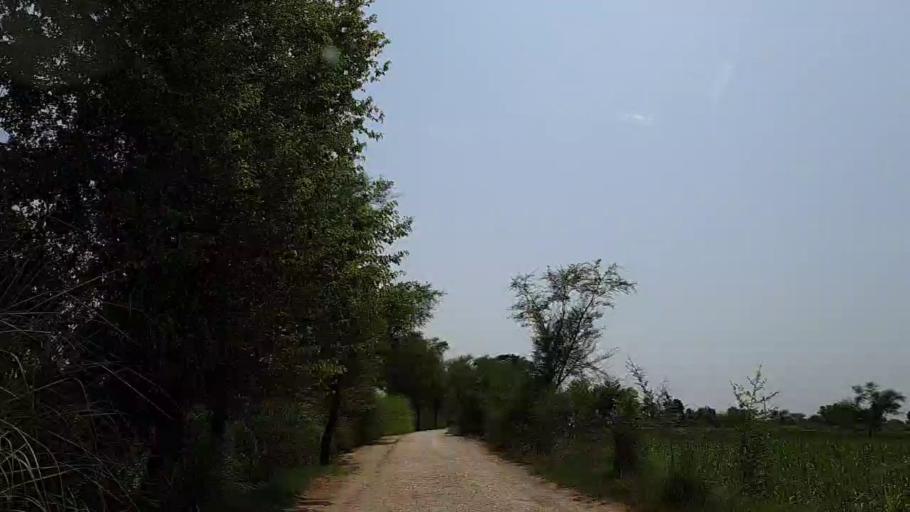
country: PK
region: Sindh
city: Adilpur
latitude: 27.9267
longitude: 69.3787
